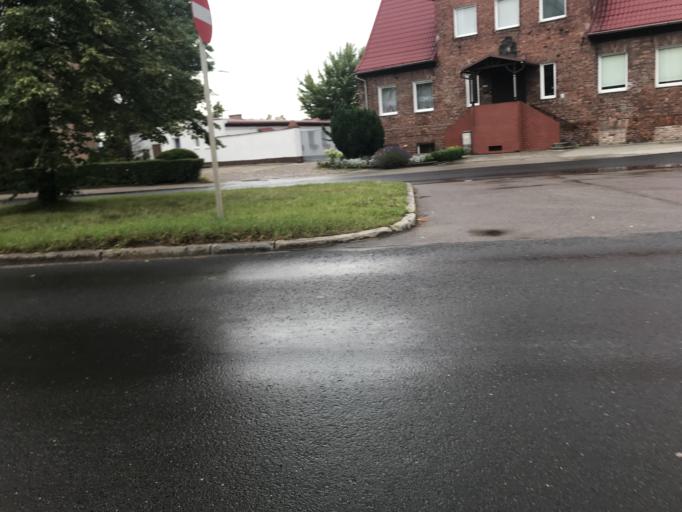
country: PL
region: Pomeranian Voivodeship
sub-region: Gdansk
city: Gdansk
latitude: 54.3499
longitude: 18.6751
